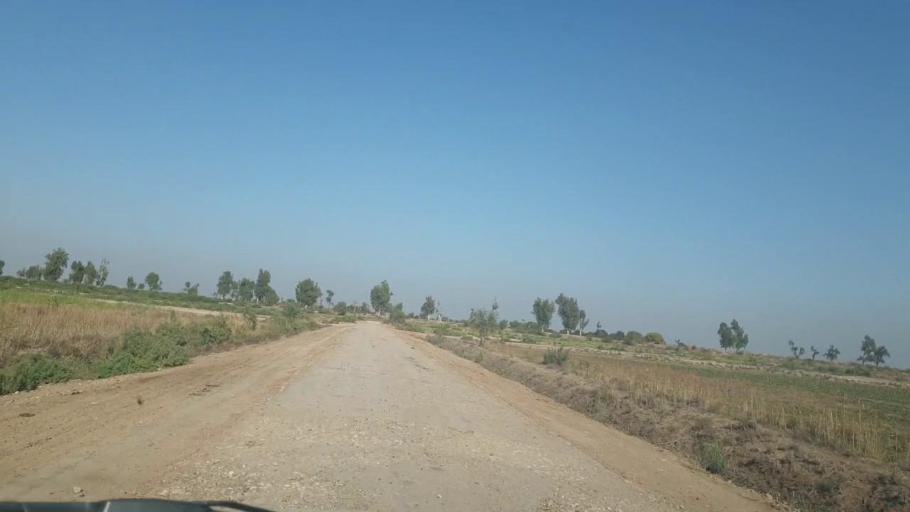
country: PK
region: Sindh
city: Mirpur Khas
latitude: 25.4530
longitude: 69.1417
